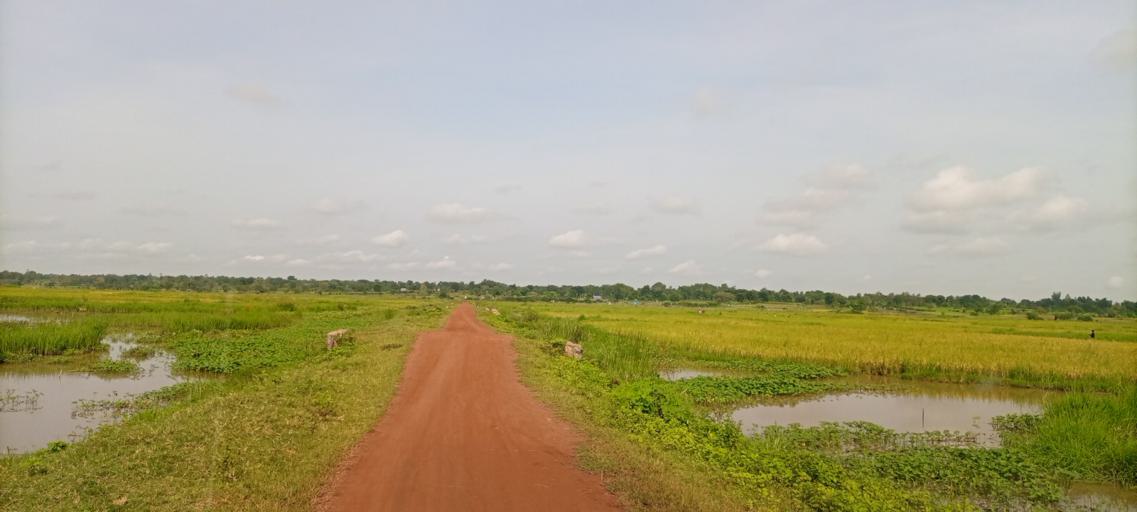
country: UG
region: Eastern Region
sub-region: Kibuku District
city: Kibuku
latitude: 1.1002
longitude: 33.7752
